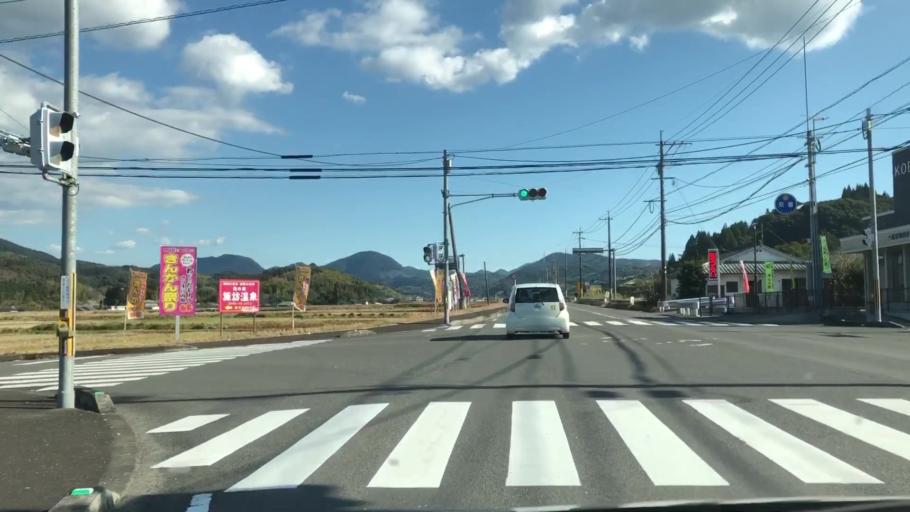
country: JP
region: Kagoshima
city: Satsumasendai
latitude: 31.7984
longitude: 130.4322
